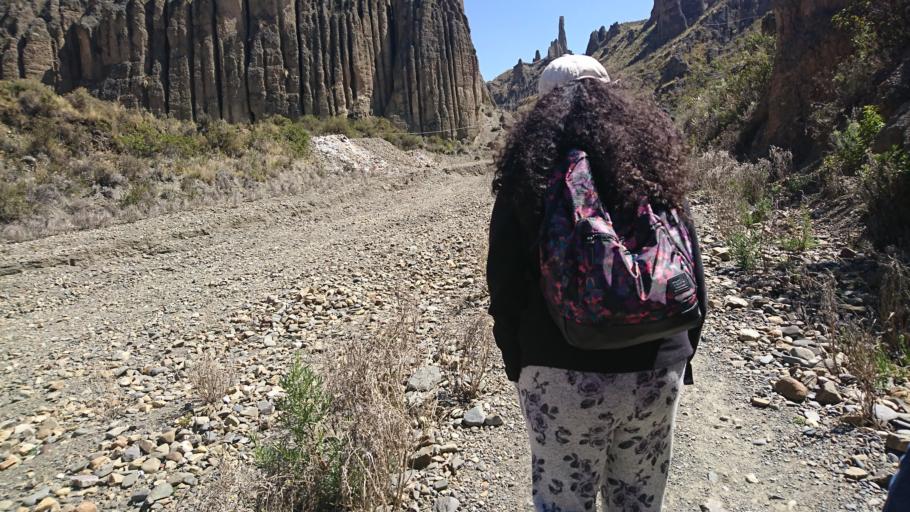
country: BO
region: La Paz
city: La Paz
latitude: -16.5420
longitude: -68.0049
